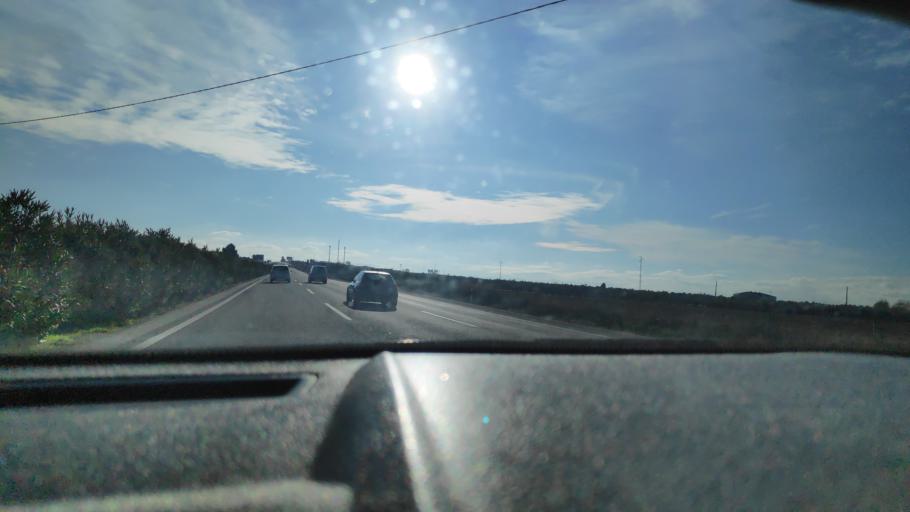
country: ES
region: Andalusia
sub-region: Province of Cordoba
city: La Carlota
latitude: 37.5986
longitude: -4.9749
